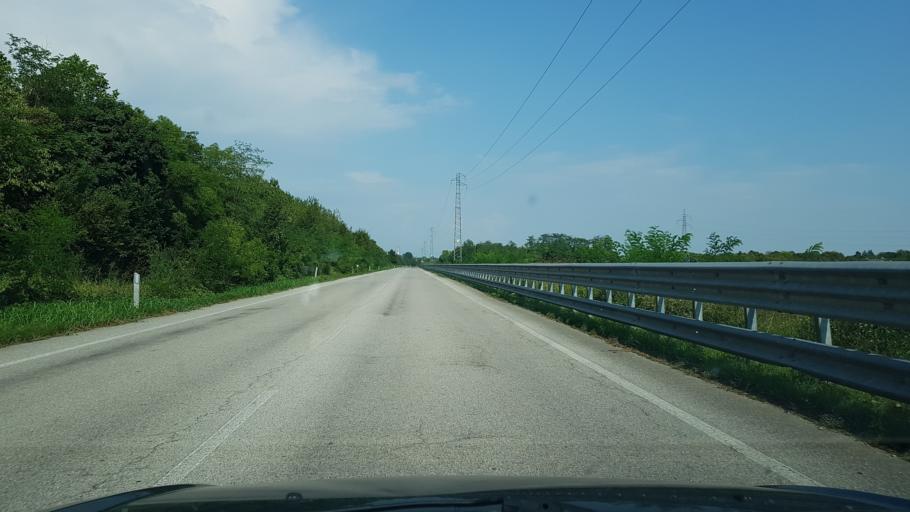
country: IT
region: Friuli Venezia Giulia
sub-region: Provincia di Pordenone
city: San Quirino
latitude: 46.0486
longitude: 12.6782
